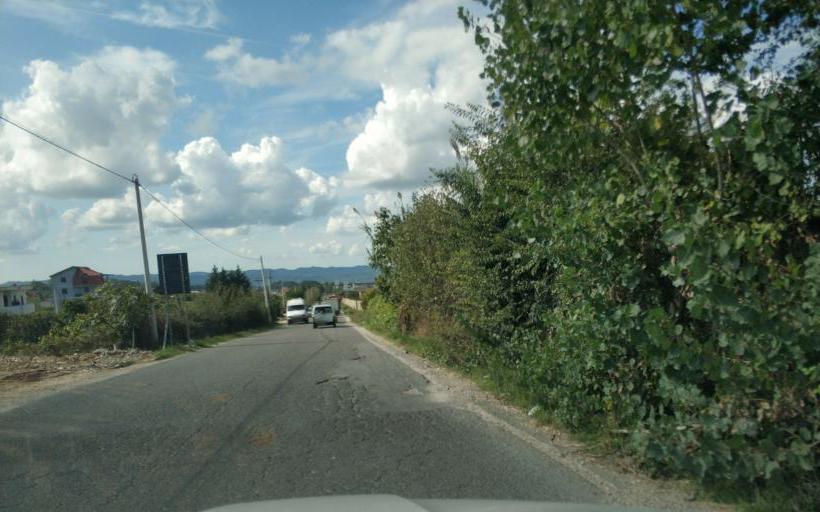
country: AL
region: Durres
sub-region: Rrethi i Krujes
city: Nikel
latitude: 41.4801
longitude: 19.7613
